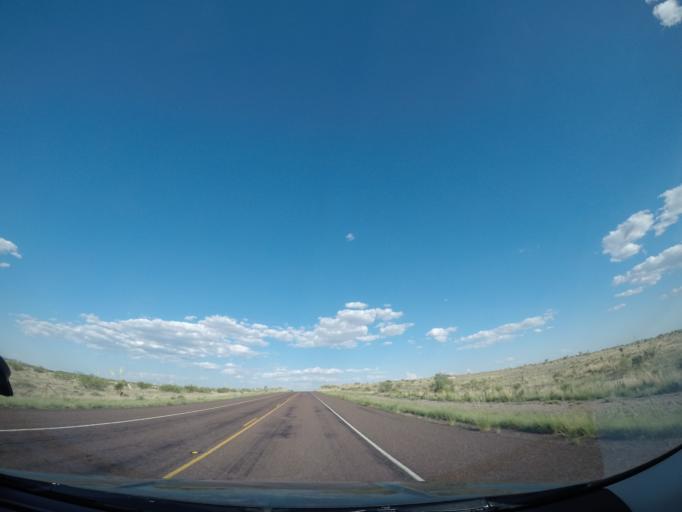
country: US
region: Texas
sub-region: Presidio County
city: Marfa
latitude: 30.3449
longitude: -104.1499
